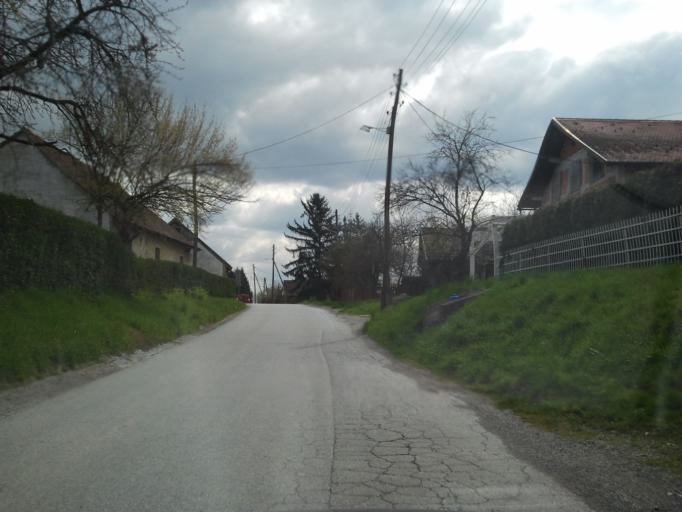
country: HR
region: Grad Zagreb
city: Brezovica
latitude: 45.7396
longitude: 15.8808
